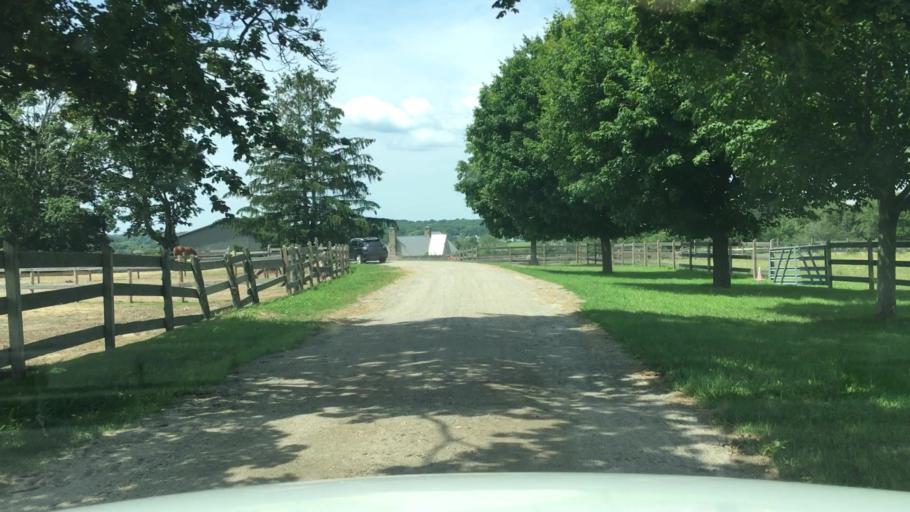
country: US
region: Maine
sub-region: Cumberland County
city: Scarborough
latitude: 43.5684
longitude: -70.2640
